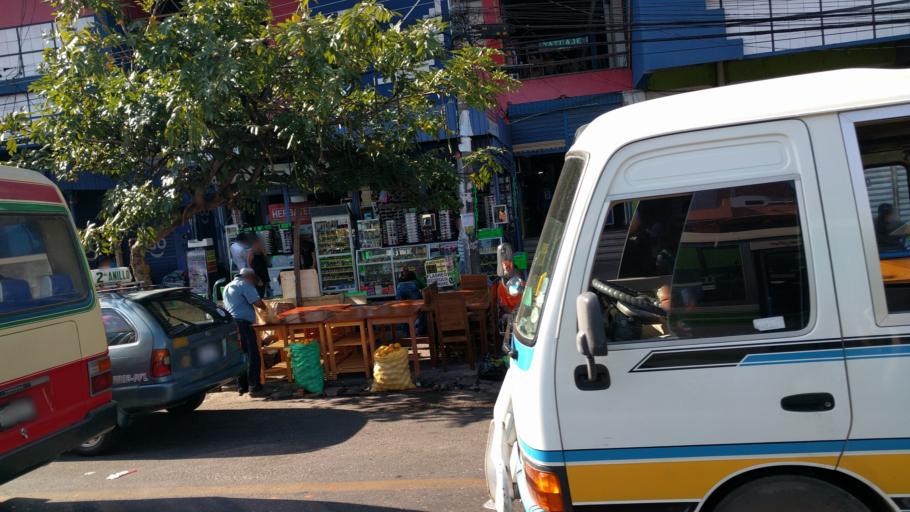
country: BO
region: Santa Cruz
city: Santa Cruz de la Sierra
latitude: -17.7946
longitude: -63.1887
